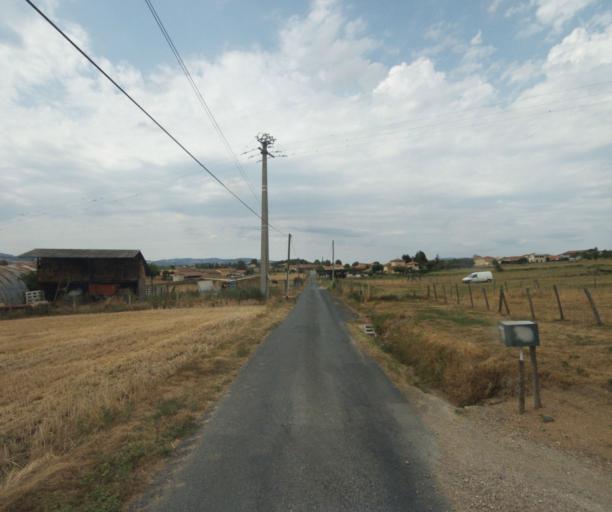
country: FR
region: Rhone-Alpes
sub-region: Departement du Rhone
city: Bully
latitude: 45.8734
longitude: 4.5576
